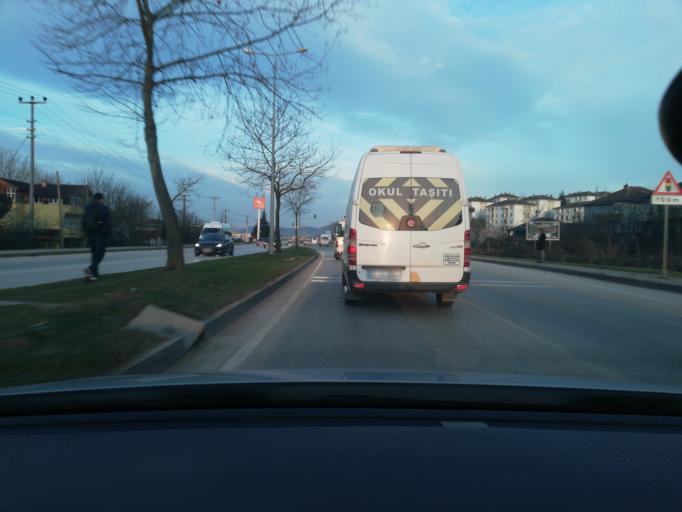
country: TR
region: Duzce
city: Konuralp
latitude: 40.9002
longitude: 31.1578
